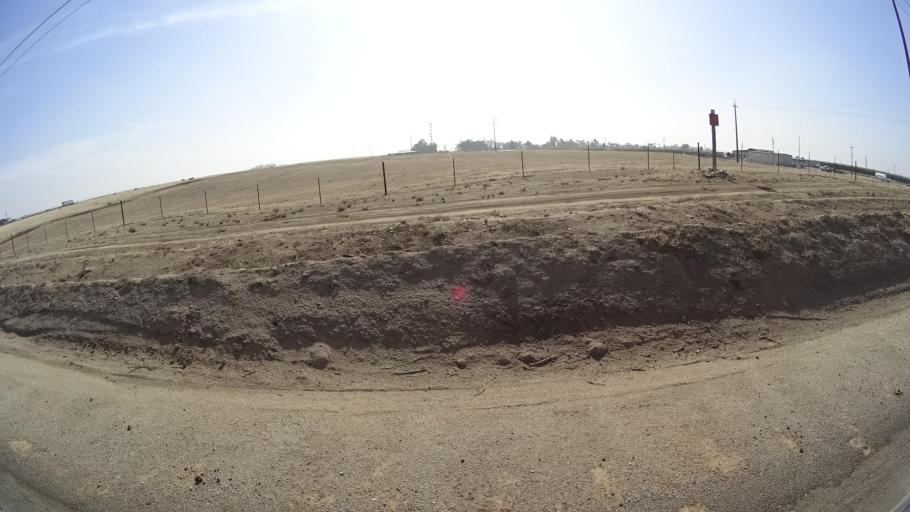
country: US
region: California
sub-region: Kern County
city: Oildale
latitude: 35.5298
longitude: -119.1071
